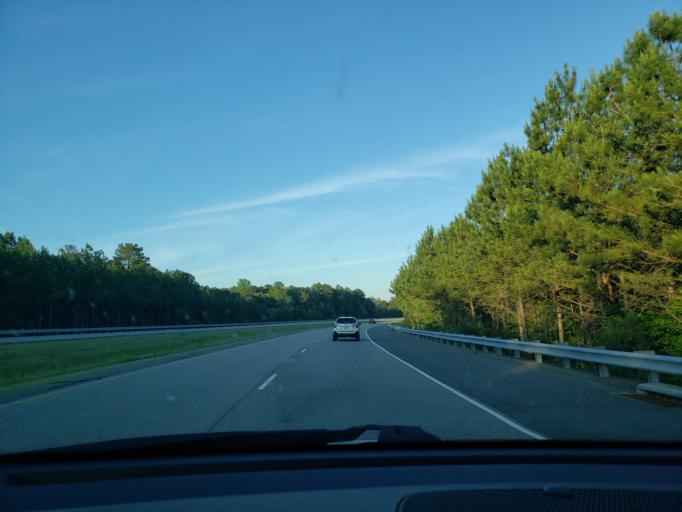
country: US
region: Virginia
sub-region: Henrico County
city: Fort Lee
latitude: 37.4793
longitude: -77.3475
